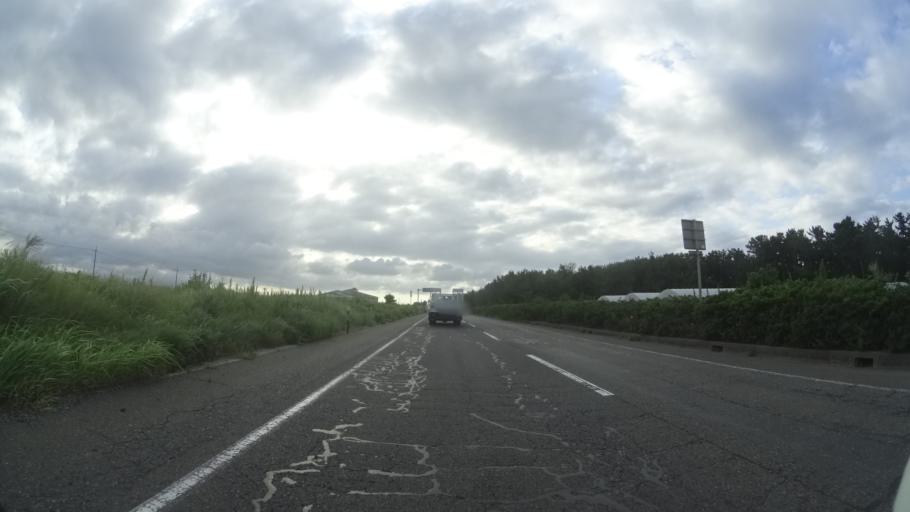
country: JP
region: Tottori
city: Kurayoshi
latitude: 35.4990
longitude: 133.7688
